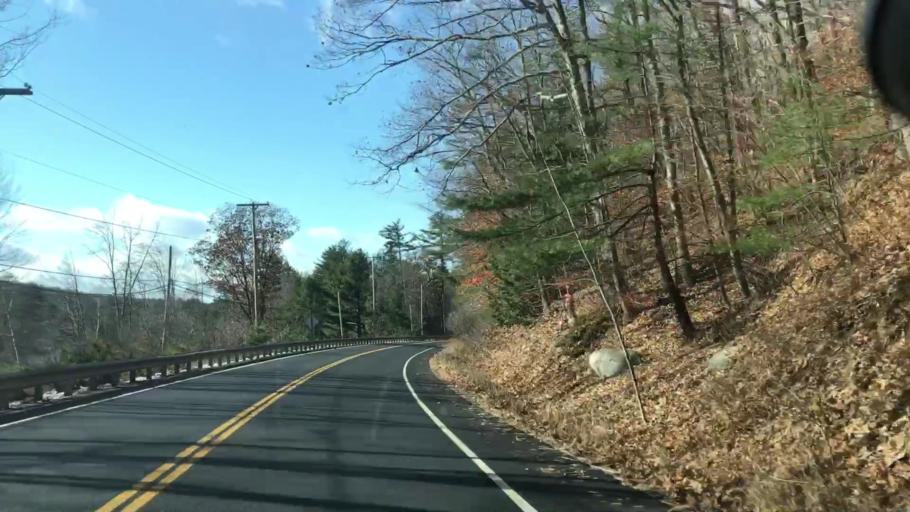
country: US
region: Maine
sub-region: Oxford County
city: Porter
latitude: 43.8053
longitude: -70.8945
